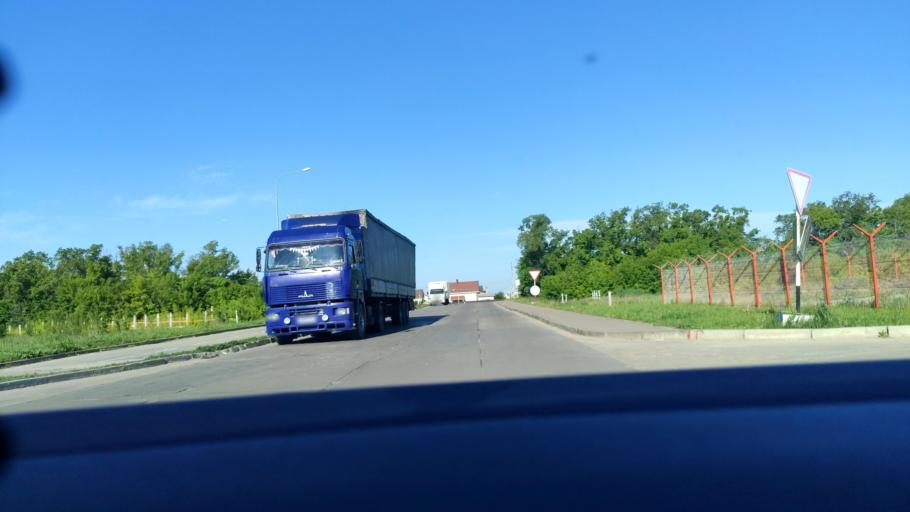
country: RU
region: Voronezj
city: Novaya Usman'
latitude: 51.6208
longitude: 39.3379
